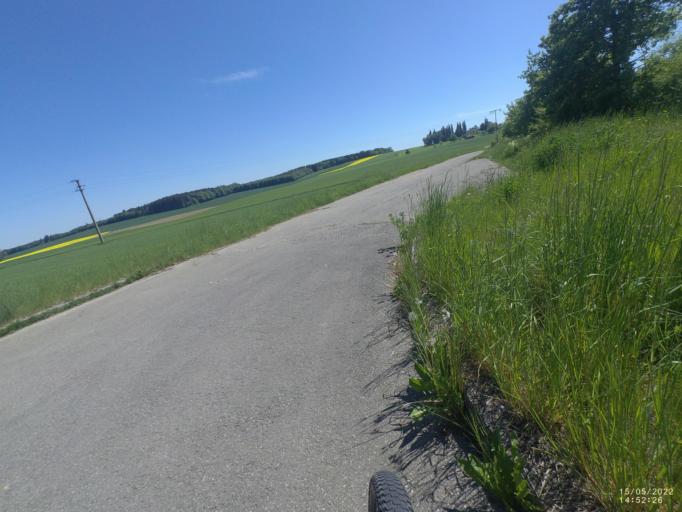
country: DE
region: Baden-Wuerttemberg
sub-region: Regierungsbezirk Stuttgart
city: Bolheim
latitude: 48.6002
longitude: 10.1385
